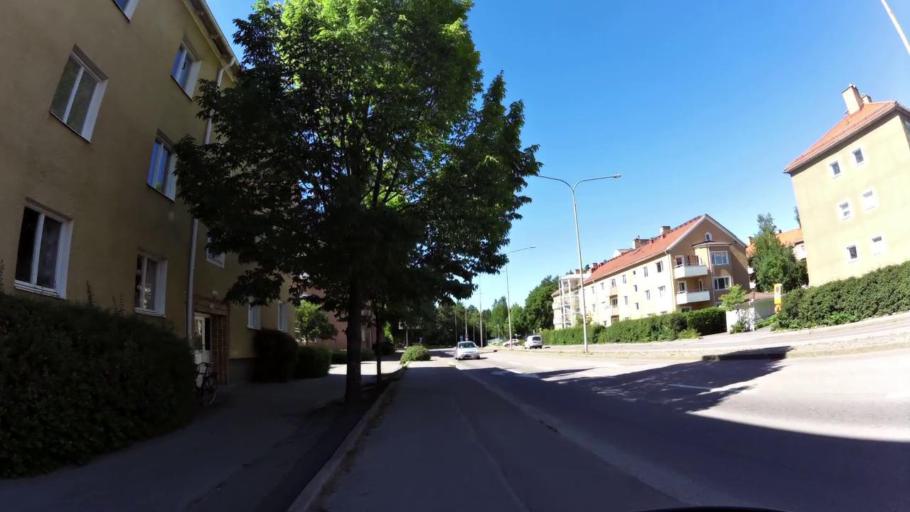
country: SE
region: OEstergoetland
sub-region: Linkopings Kommun
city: Linkoping
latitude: 58.3979
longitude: 15.6377
